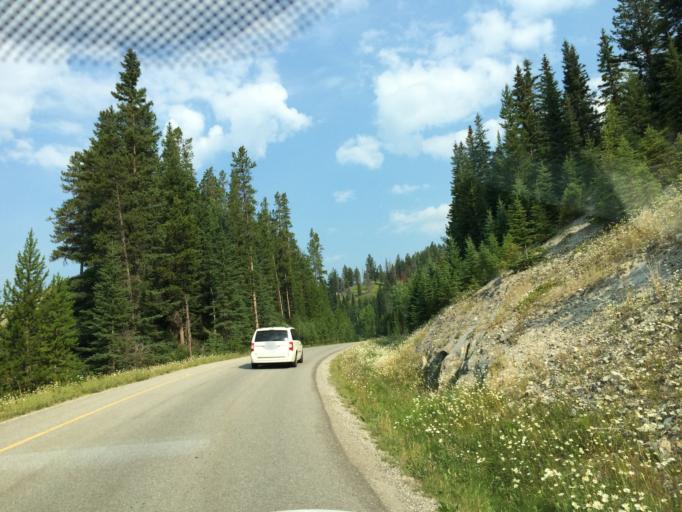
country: CA
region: Alberta
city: Banff
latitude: 51.1700
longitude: -115.6985
